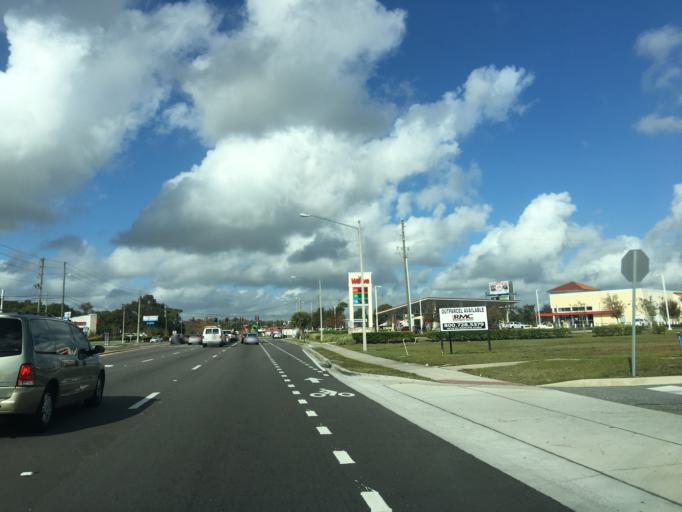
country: US
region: Florida
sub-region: Orange County
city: Azalea Park
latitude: 28.5150
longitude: -81.2883
